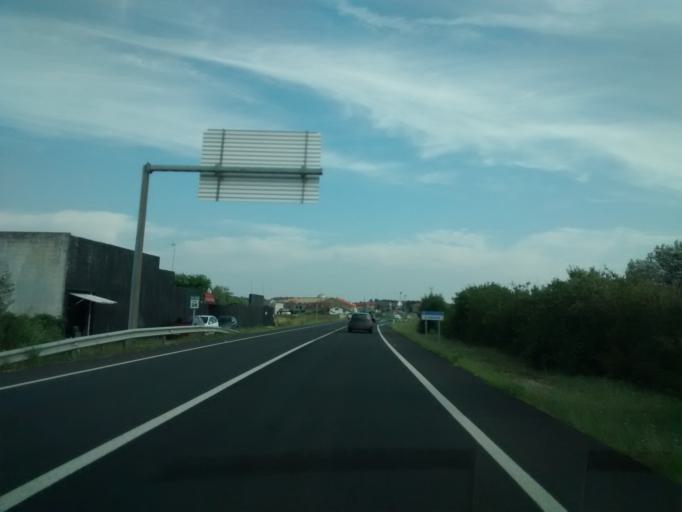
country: ES
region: Galicia
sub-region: Provincia de Pontevedra
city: O Grove
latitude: 42.4430
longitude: -8.8683
